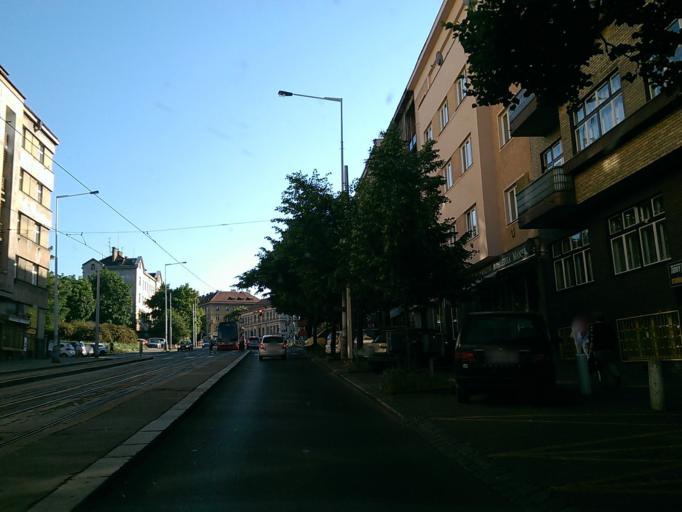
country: CZ
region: Praha
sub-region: Praha 2
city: Vysehrad
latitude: 50.0618
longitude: 14.4373
